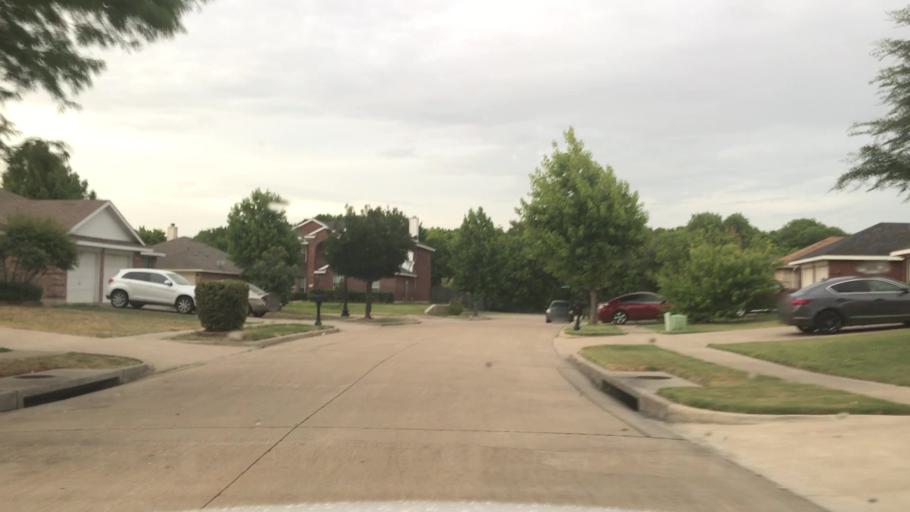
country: US
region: Texas
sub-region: Kaufman County
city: Forney
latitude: 32.7202
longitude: -96.5357
